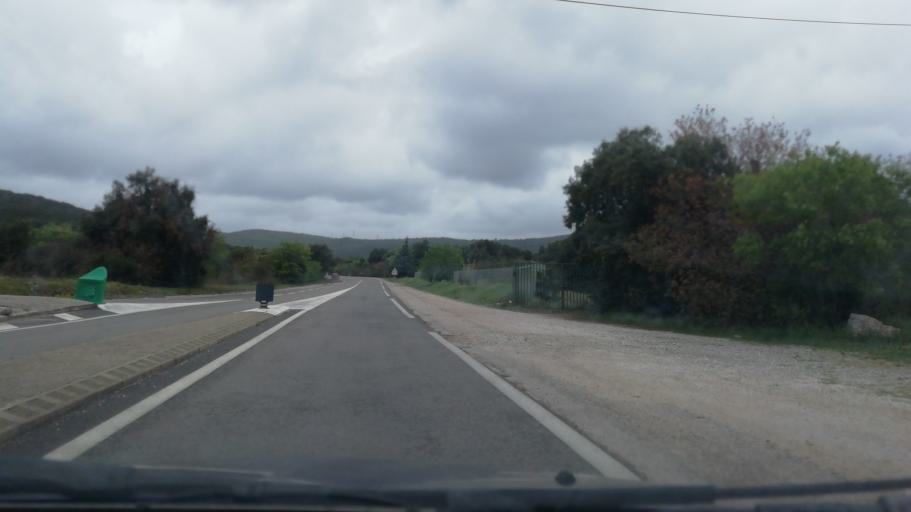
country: FR
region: Languedoc-Roussillon
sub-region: Departement de l'Herault
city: Les Matelles
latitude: 43.7307
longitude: 3.7951
